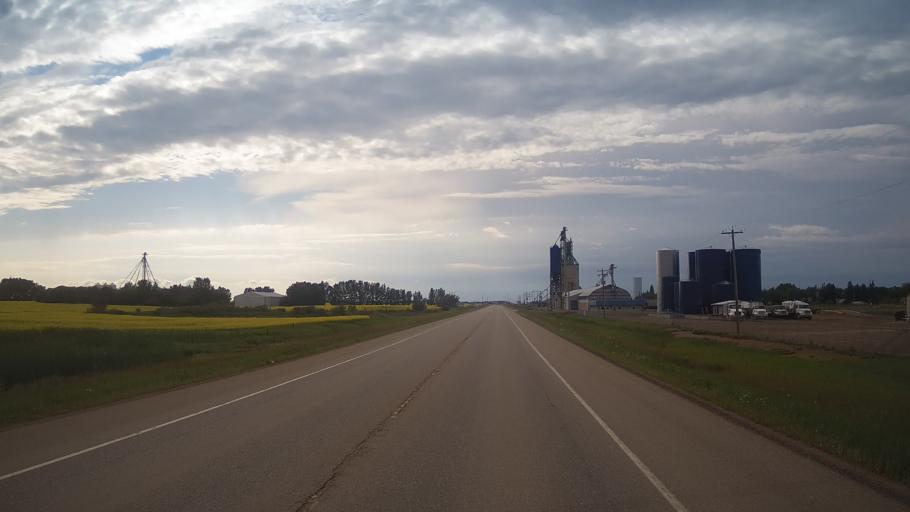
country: CA
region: Alberta
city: Viking
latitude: 53.0890
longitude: -111.7698
